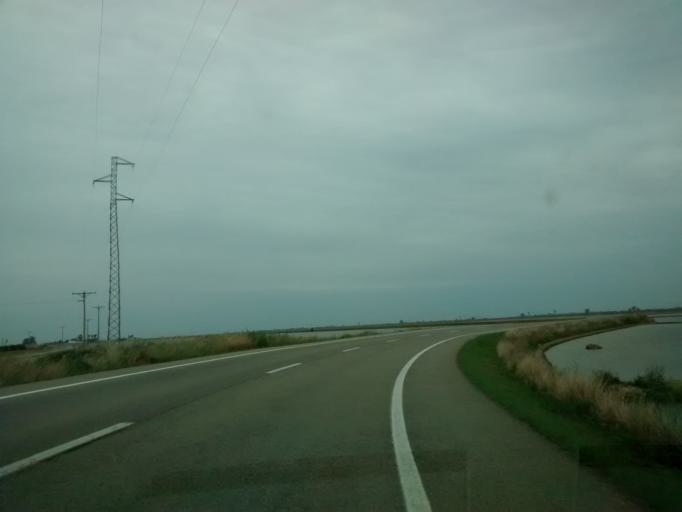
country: ES
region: Catalonia
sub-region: Provincia de Tarragona
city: Deltebre
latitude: 40.6934
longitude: 0.6827
